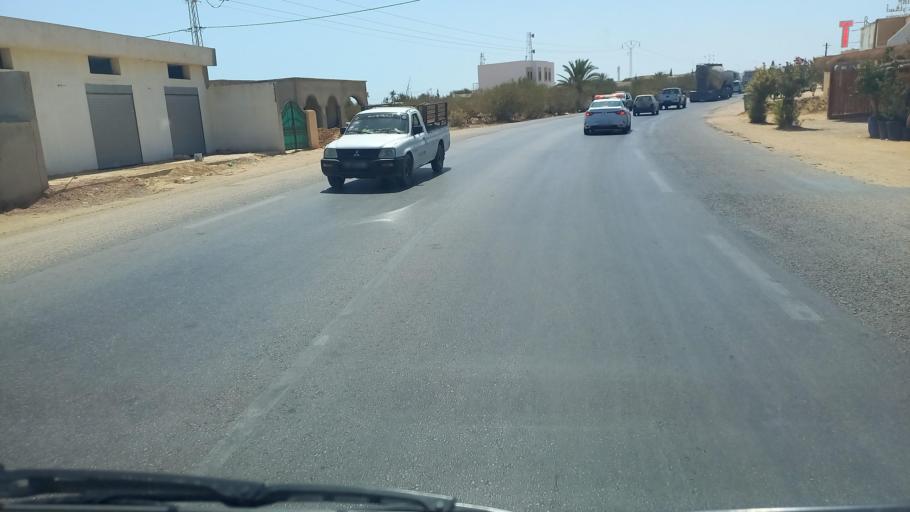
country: TN
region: Madanin
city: Houmt Souk
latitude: 33.8081
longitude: 10.8808
